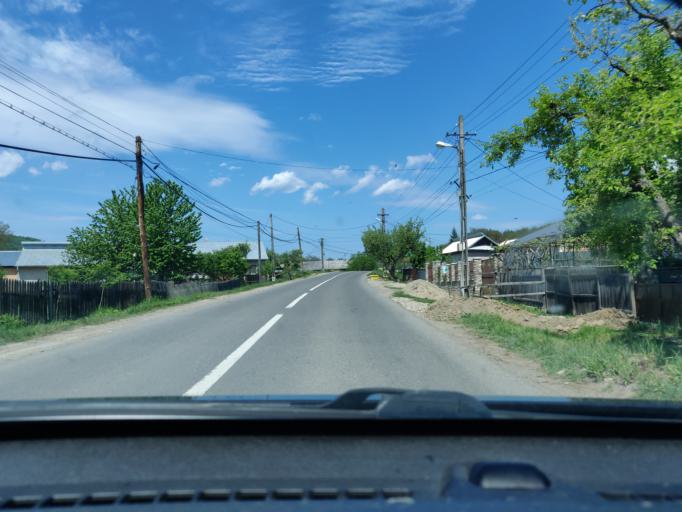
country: RO
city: Campurile de Jos
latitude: 46.0186
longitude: 26.7794
